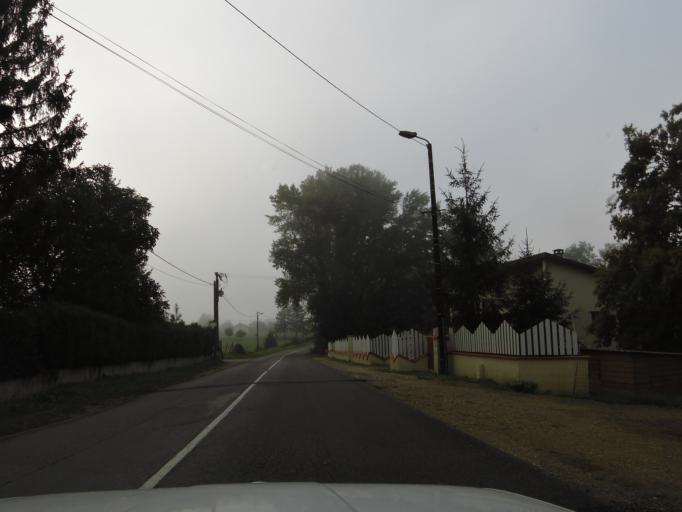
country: FR
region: Rhone-Alpes
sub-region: Departement de l'Isere
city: Creys-Mepieu
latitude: 45.7827
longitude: 5.4681
